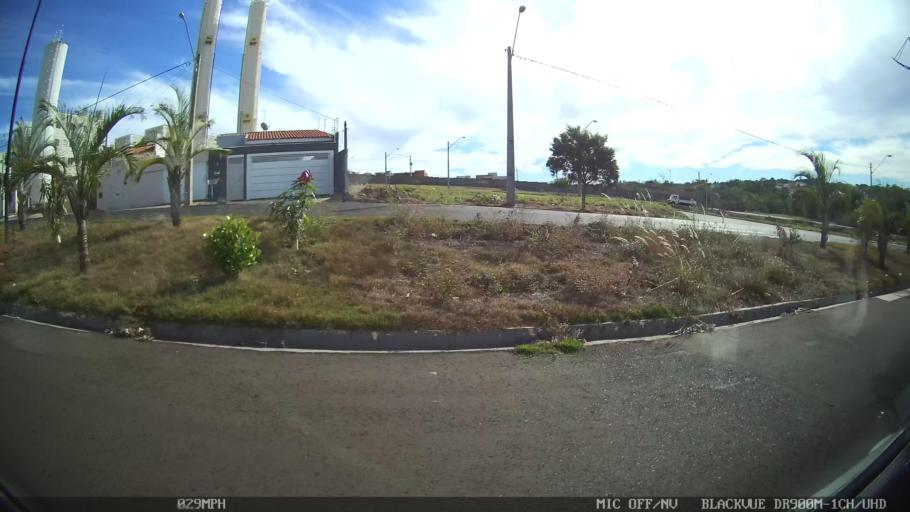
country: BR
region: Sao Paulo
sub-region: Catanduva
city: Catanduva
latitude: -21.1205
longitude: -48.9749
